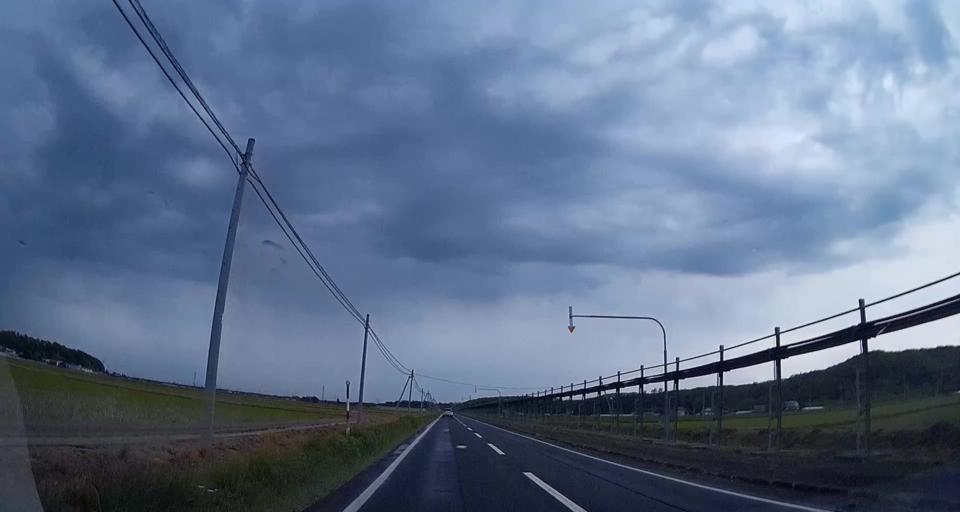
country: JP
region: Hokkaido
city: Chitose
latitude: 42.7169
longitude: 141.8653
